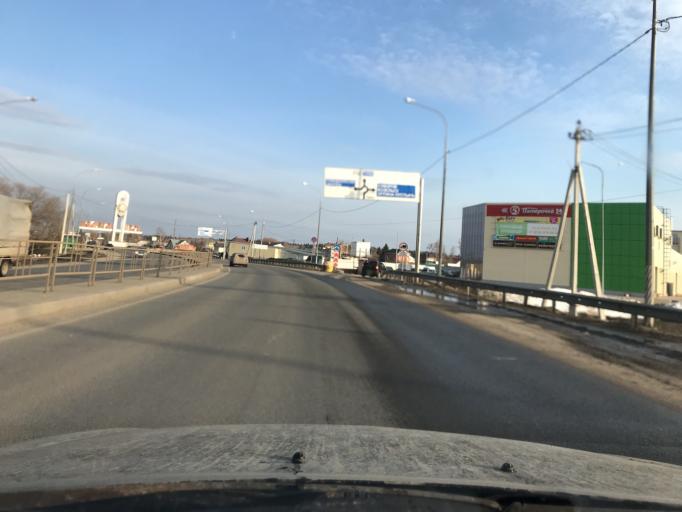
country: RU
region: Kaluga
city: Kaluga
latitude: 54.4698
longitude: 36.2368
